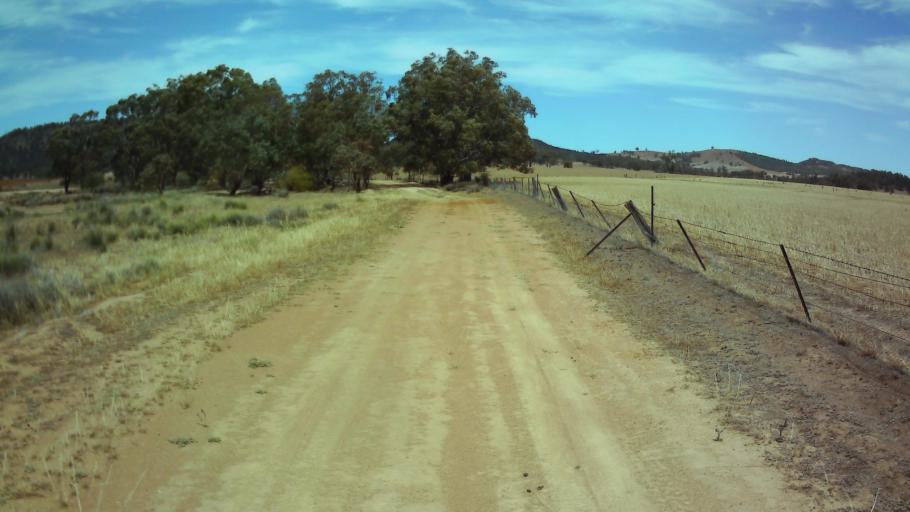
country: AU
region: New South Wales
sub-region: Weddin
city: Grenfell
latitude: -33.7627
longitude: 148.1461
